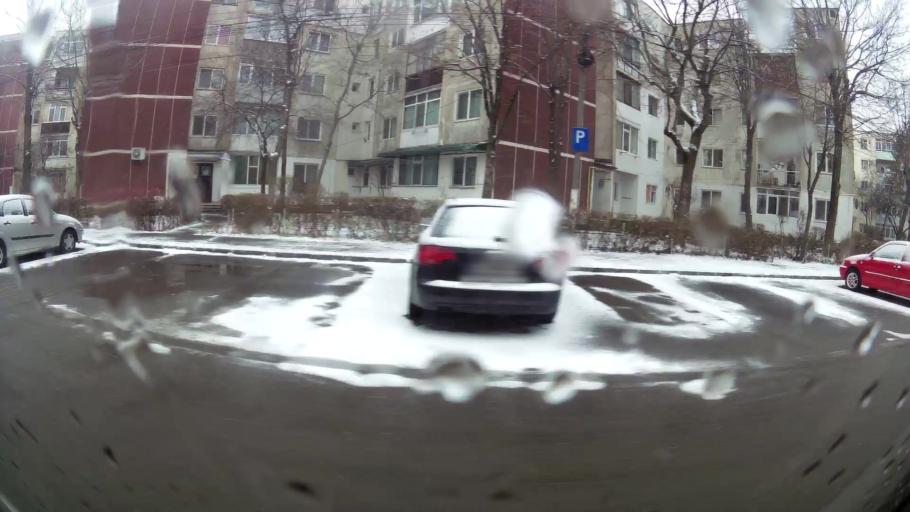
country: RO
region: Prahova
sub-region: Comuna Targsoru Vechi
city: Strejnicu
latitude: 44.9326
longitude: 25.9831
